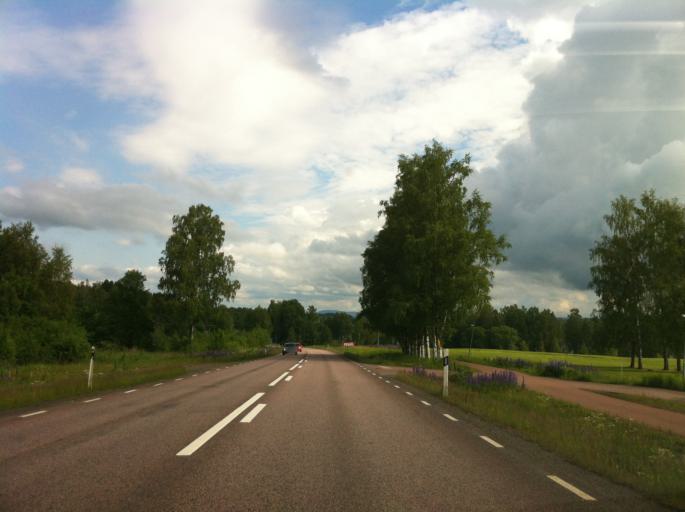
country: SE
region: Vaermland
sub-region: Sunne Kommun
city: Sunne
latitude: 59.8092
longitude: 13.1257
